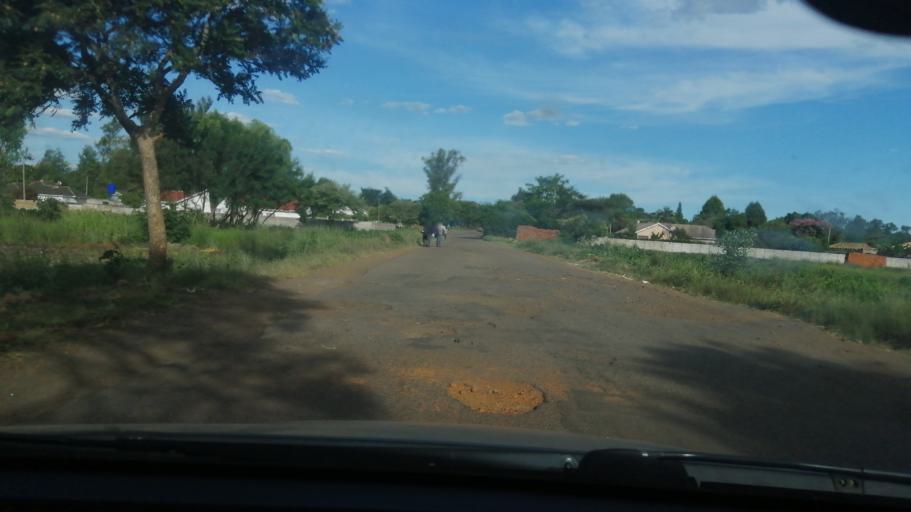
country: ZW
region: Harare
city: Harare
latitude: -17.7637
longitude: 31.0641
